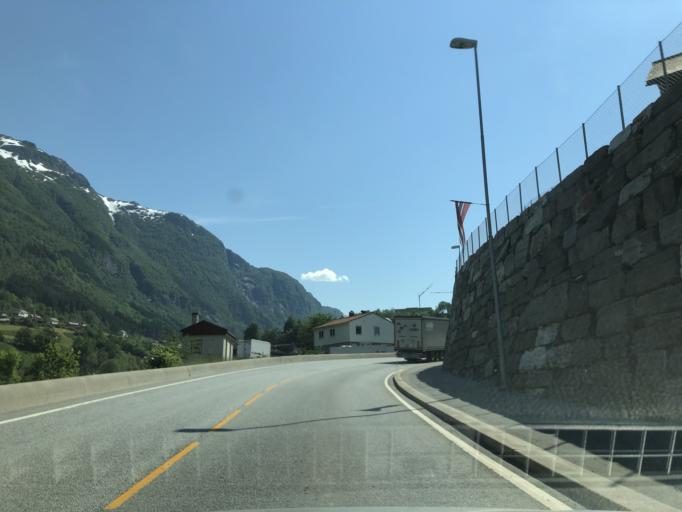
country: NO
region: Hordaland
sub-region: Odda
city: Odda
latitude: 60.0606
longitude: 6.5489
